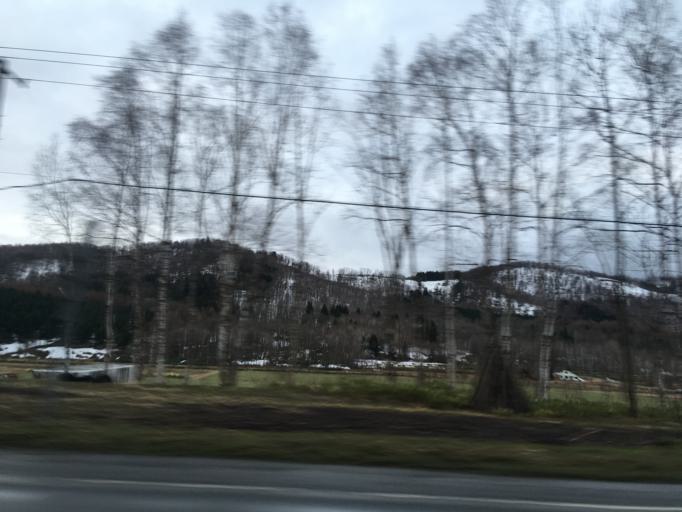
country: JP
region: Hokkaido
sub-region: Asahikawa-shi
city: Asahikawa
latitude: 43.9470
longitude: 142.4585
